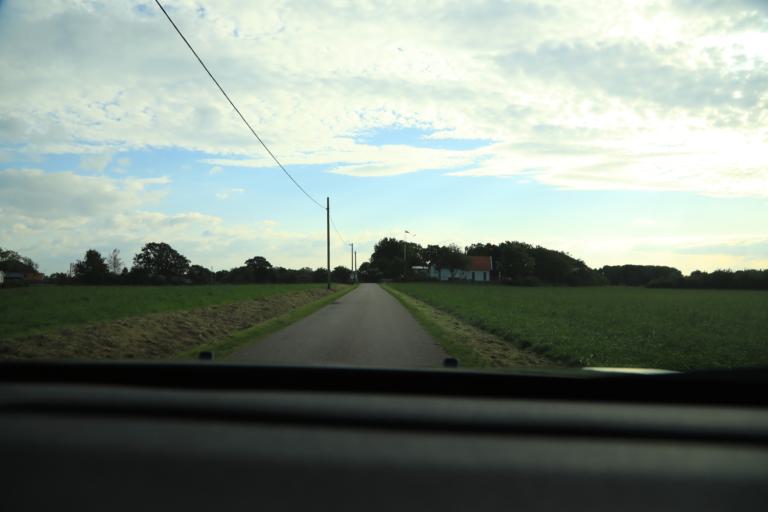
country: SE
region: Halland
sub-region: Varbergs Kommun
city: Traslovslage
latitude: 57.0423
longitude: 12.3039
